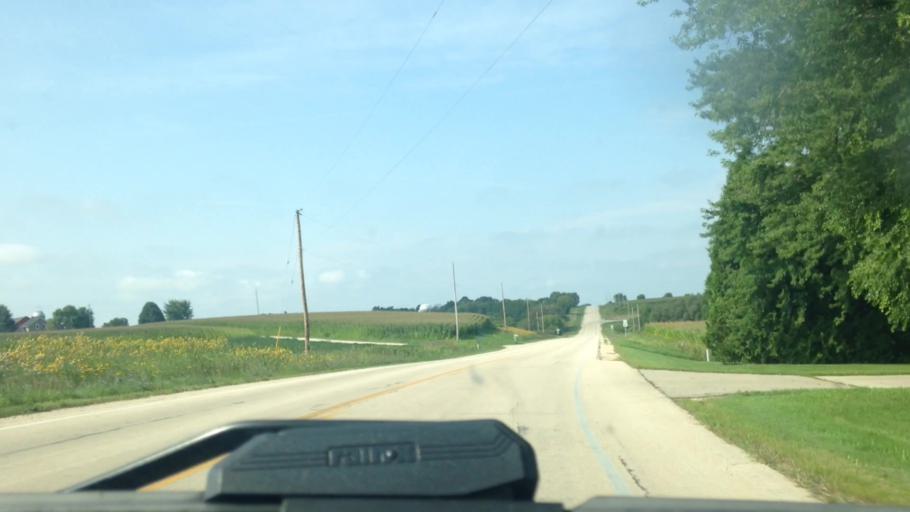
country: US
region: Wisconsin
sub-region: Dodge County
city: Theresa
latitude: 43.5322
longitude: -88.4981
